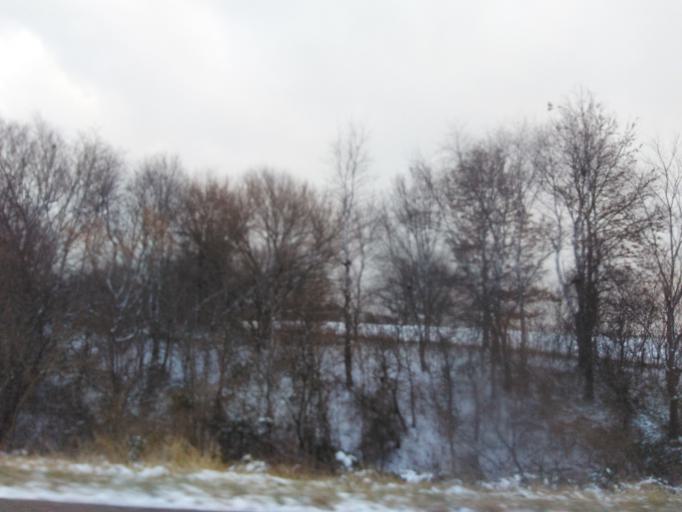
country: US
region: Illinois
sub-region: Madison County
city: Highland
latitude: 38.8221
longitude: -89.5579
